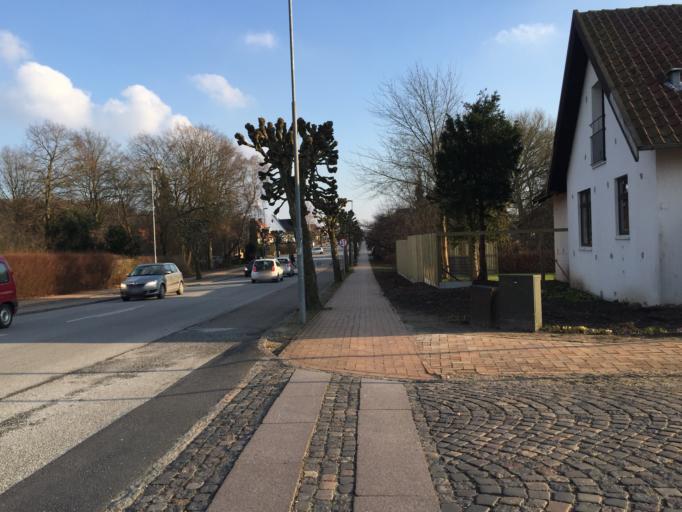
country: DK
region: South Denmark
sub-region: Odense Kommune
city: Odense
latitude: 55.3856
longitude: 10.4039
